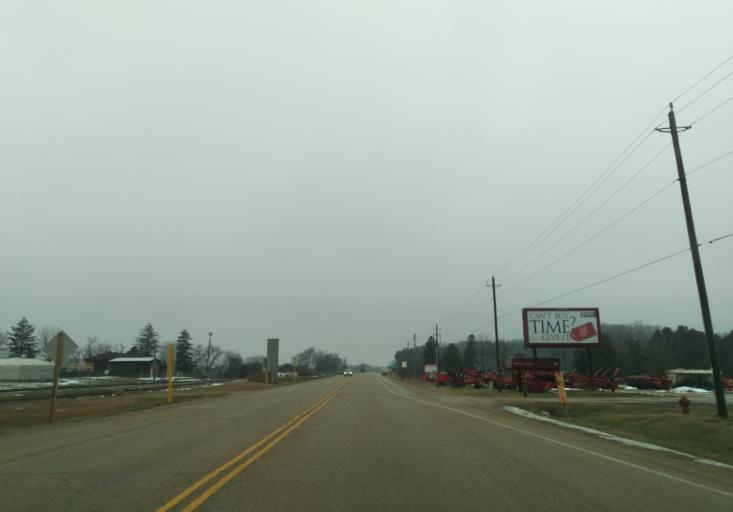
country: US
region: Wisconsin
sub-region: Dane County
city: Cross Plains
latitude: 43.1148
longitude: -89.6616
